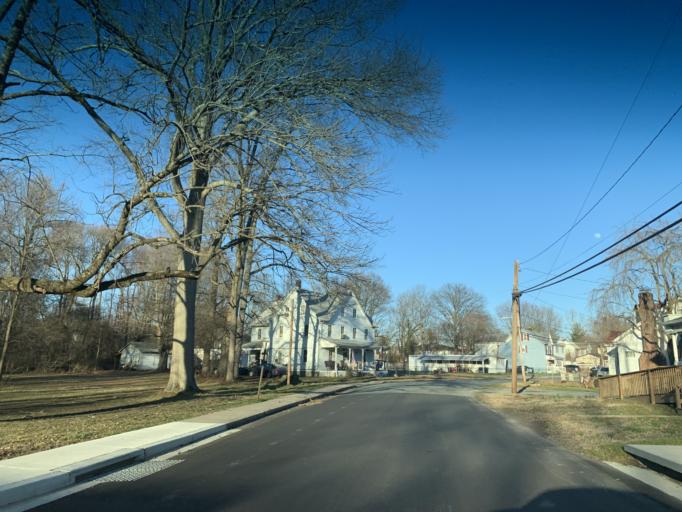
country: US
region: Maryland
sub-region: Cecil County
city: Perryville
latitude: 39.5613
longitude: -76.0736
